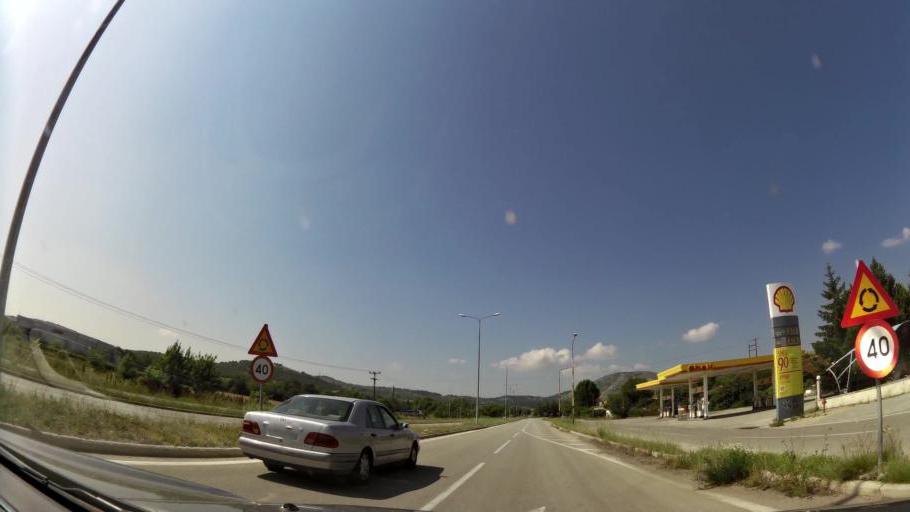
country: GR
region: West Macedonia
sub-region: Nomos Kozanis
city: Koila
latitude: 40.3387
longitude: 21.7932
